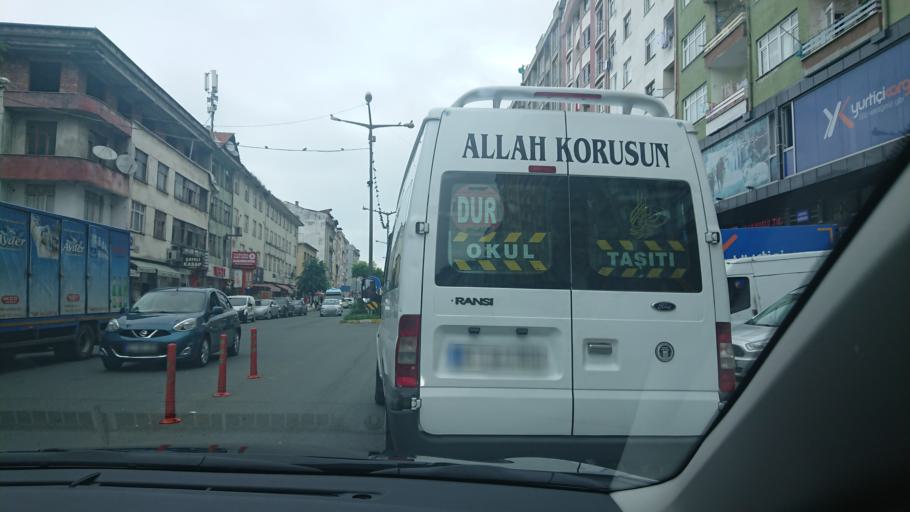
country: TR
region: Rize
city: Cayeli
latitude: 41.0860
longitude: 40.7230
